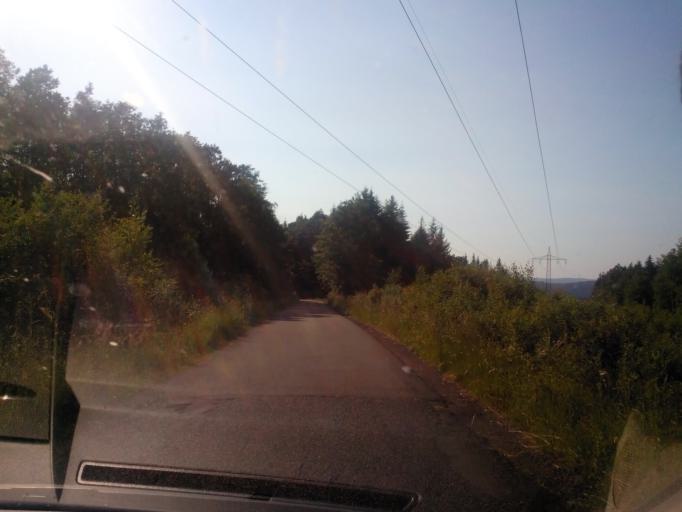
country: DE
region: Saarland
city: Nalbach
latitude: 49.4206
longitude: 6.7927
